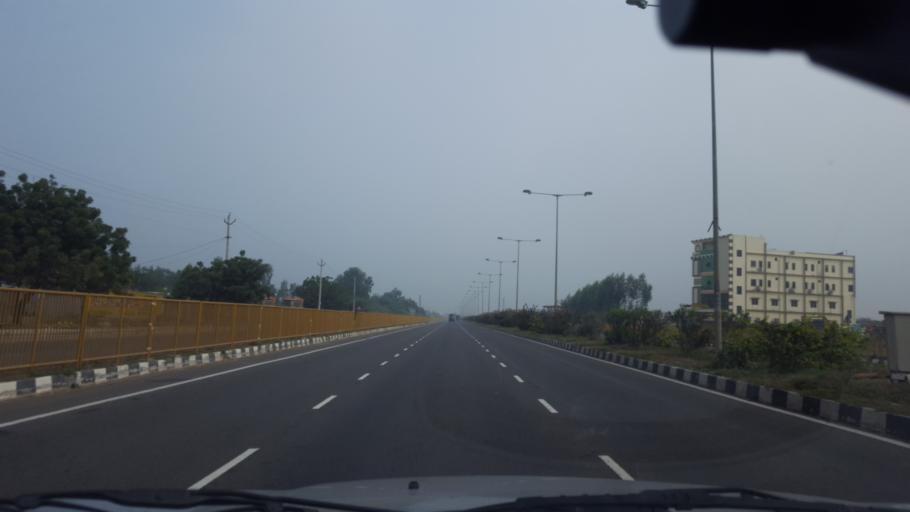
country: IN
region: Andhra Pradesh
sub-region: Guntur
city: Chilakalurupet
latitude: 15.9986
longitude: 80.1103
